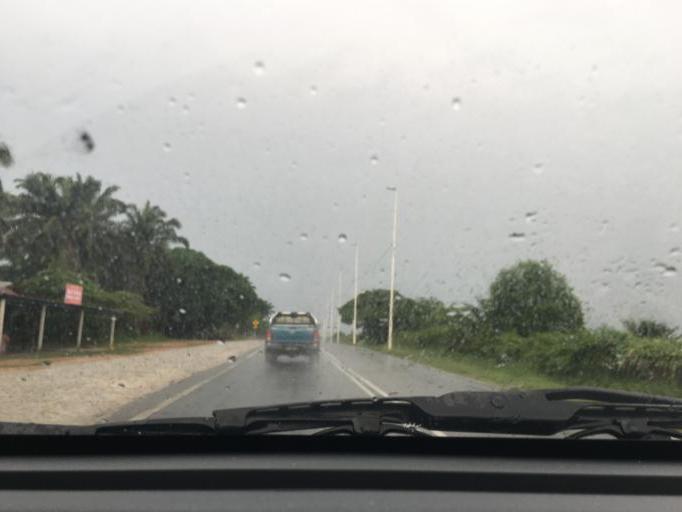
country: MY
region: Kedah
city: Sungai Petani
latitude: 5.5986
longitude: 100.6396
